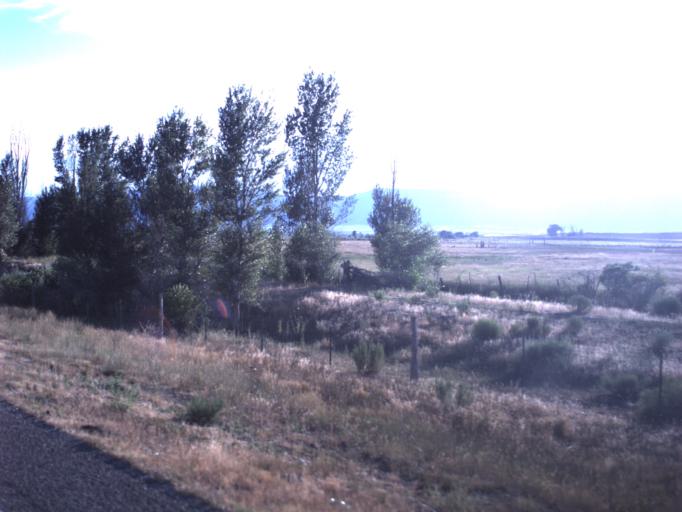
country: US
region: Utah
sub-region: Sanpete County
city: Mount Pleasant
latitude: 39.5007
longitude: -111.5046
